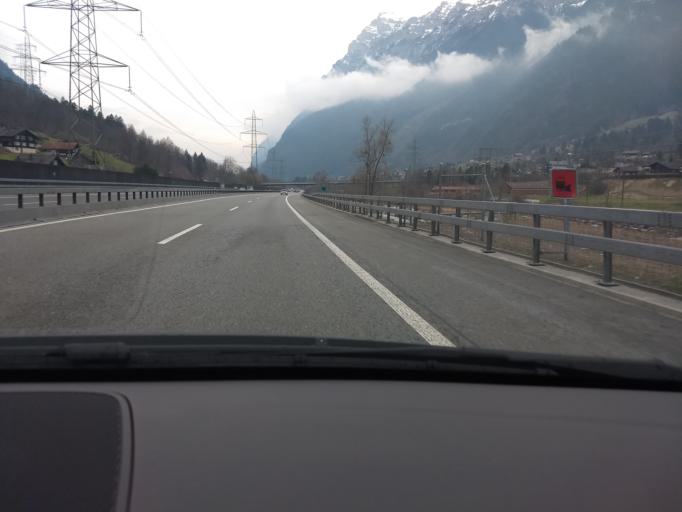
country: CH
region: Uri
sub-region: Uri
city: Silenen
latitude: 46.7911
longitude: 8.6660
